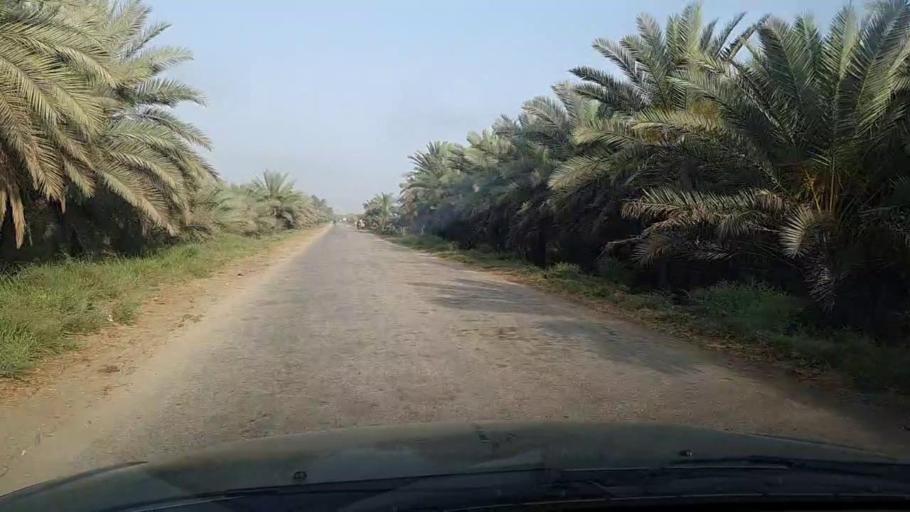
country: PK
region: Sindh
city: Pir jo Goth
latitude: 27.5536
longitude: 68.6858
